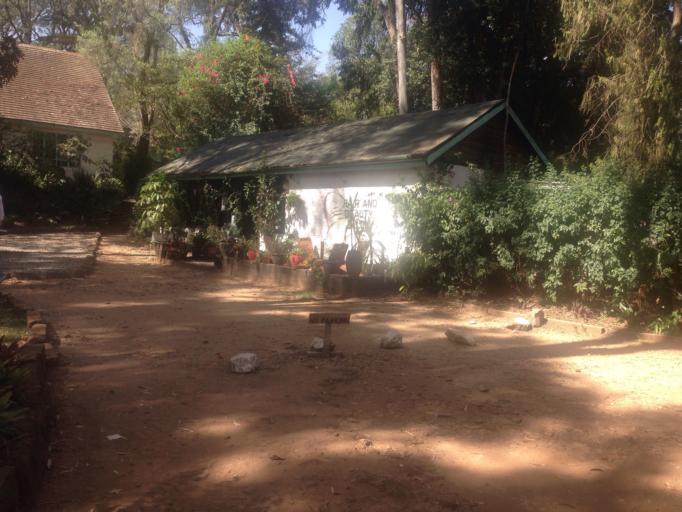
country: KE
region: Kajiado
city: Ngong
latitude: -1.3201
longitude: 36.7058
